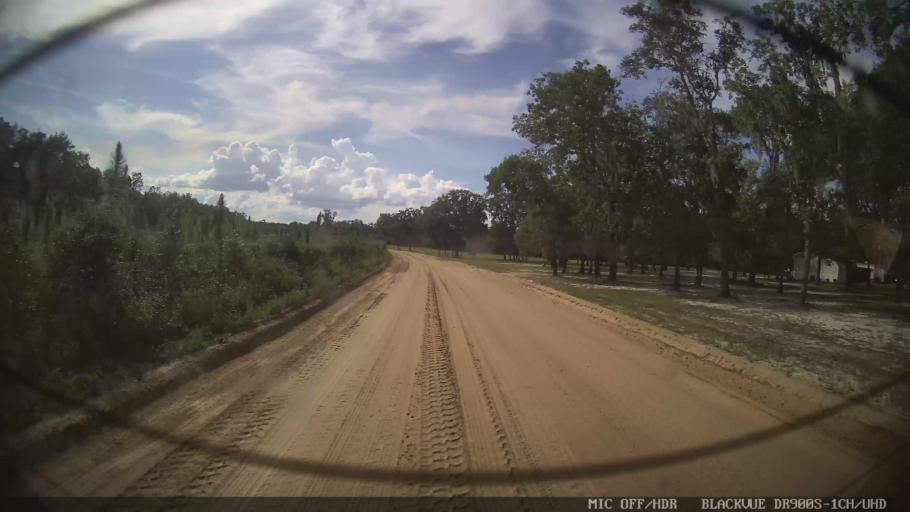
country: US
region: Georgia
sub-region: Echols County
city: Statenville
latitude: 30.6233
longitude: -83.1872
